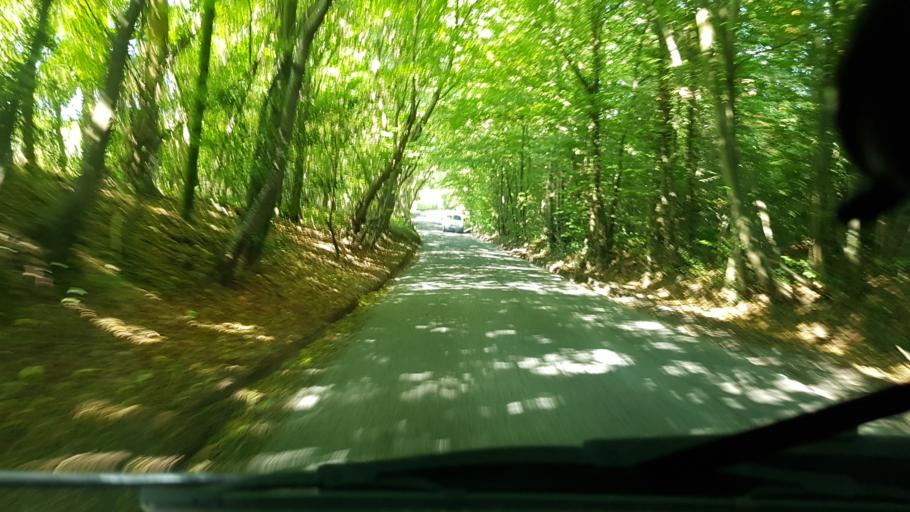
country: GB
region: England
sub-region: Surrey
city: Ockley
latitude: 51.1009
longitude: -0.3636
